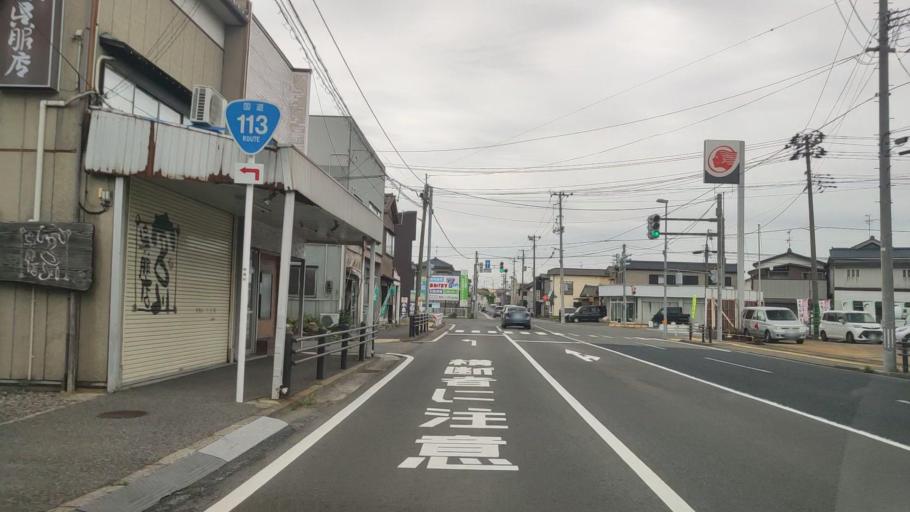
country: JP
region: Niigata
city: Niigata-shi
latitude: 37.9329
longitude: 139.0723
